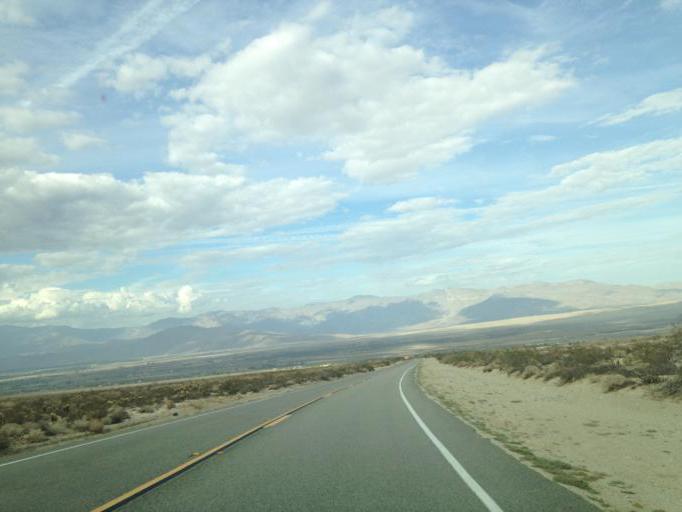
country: US
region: California
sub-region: San Diego County
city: Borrego Springs
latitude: 33.1720
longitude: -116.3353
